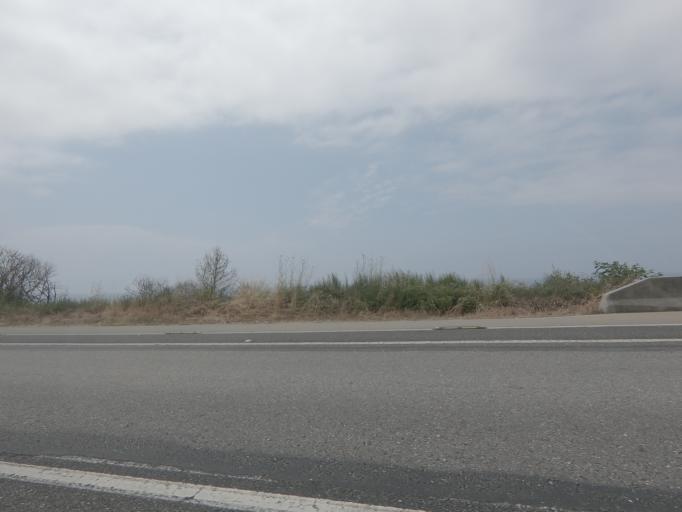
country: ES
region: Galicia
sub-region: Provincia de Pontevedra
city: Oia
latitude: 41.9780
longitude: -8.8849
